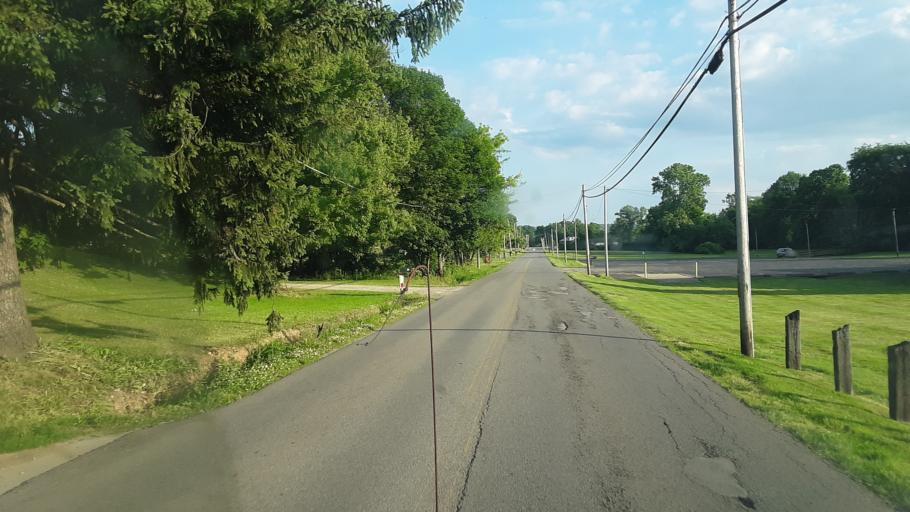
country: US
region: Ohio
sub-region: Richland County
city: Lincoln Heights
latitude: 40.7602
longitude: -82.4748
